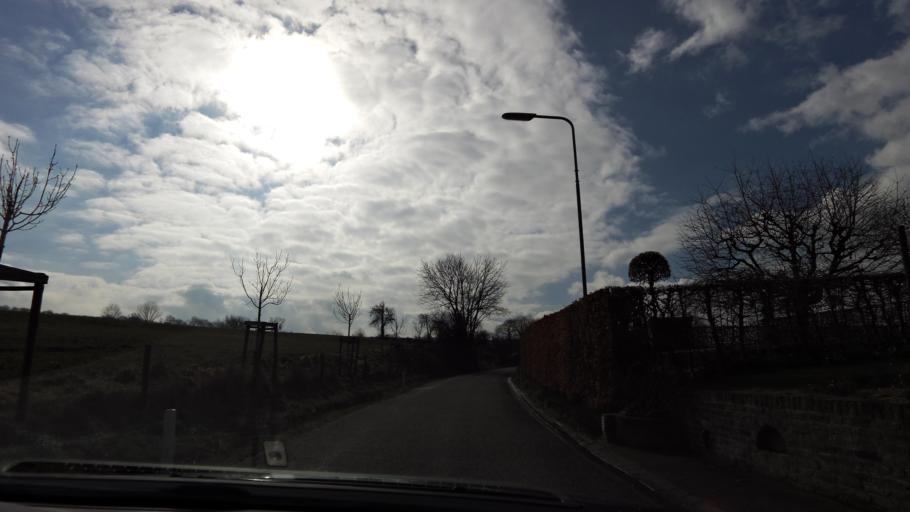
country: BE
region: Wallonia
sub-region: Province de Liege
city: Plombieres
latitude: 50.7881
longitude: 5.9290
